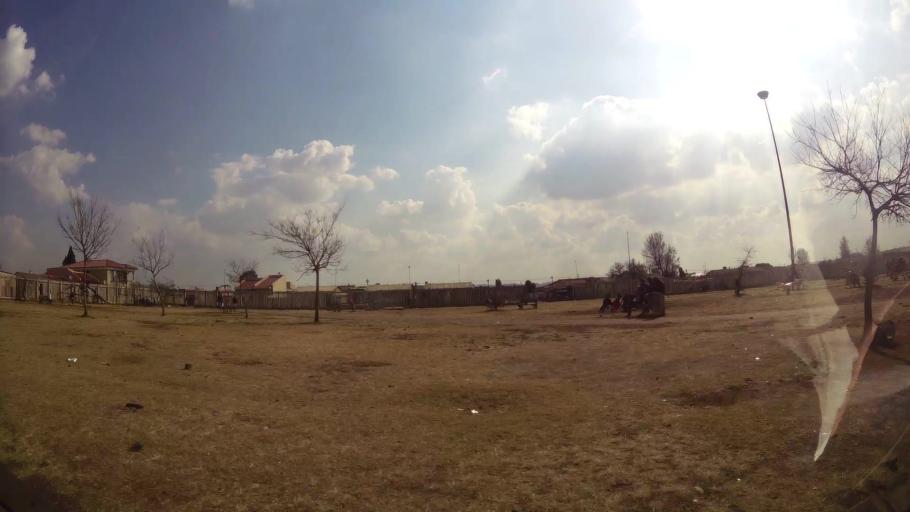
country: ZA
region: Gauteng
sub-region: Ekurhuleni Metropolitan Municipality
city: Germiston
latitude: -26.3070
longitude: 28.1502
